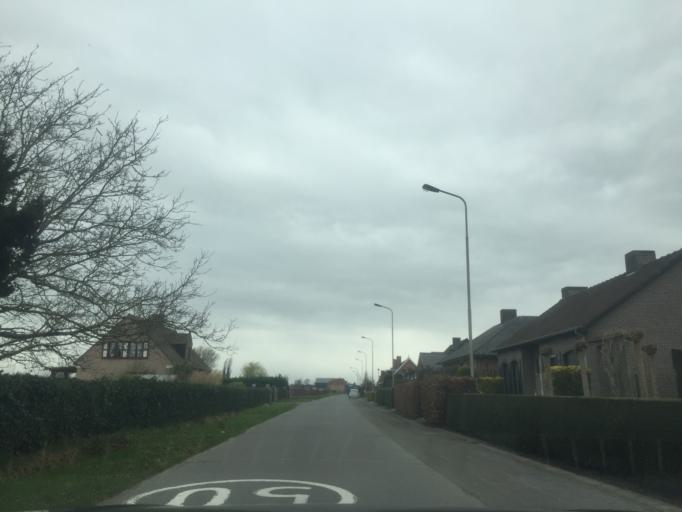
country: BE
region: Flanders
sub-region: Provincie West-Vlaanderen
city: Oostrozebeke
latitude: 50.9183
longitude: 3.3247
